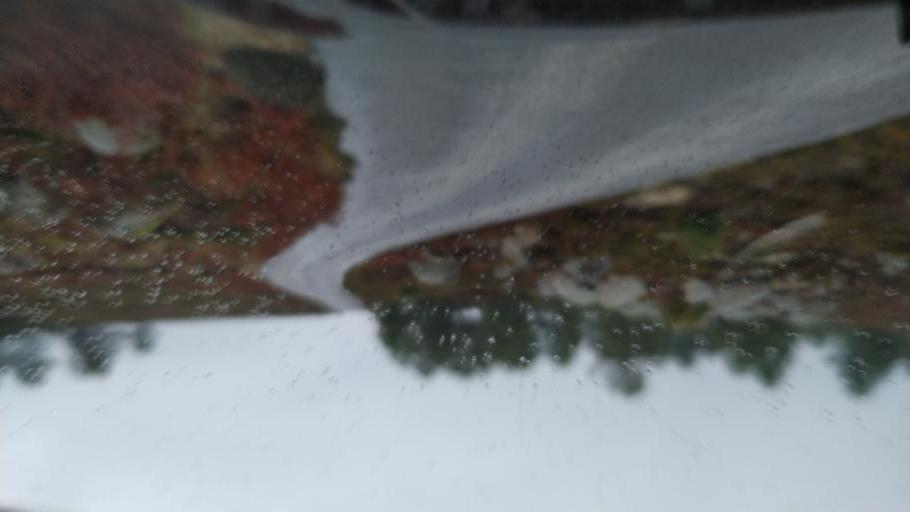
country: PT
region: Vila Real
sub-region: Vila Real
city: Vila Real
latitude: 41.3286
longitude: -7.7881
